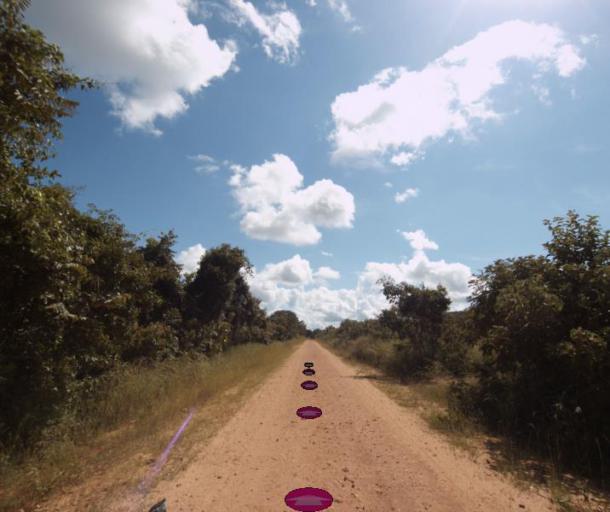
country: BR
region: Goias
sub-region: Pirenopolis
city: Pirenopolis
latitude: -15.7744
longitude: -49.0026
